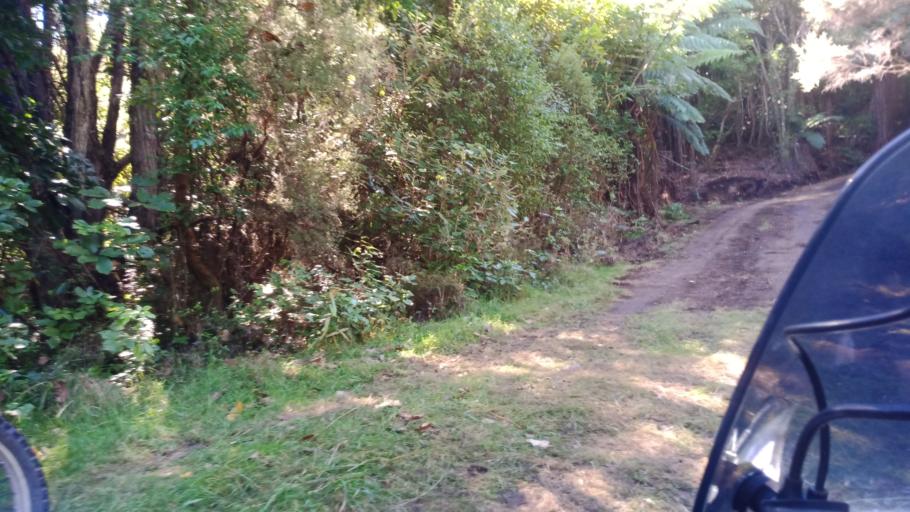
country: NZ
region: Hawke's Bay
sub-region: Wairoa District
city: Wairoa
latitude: -39.0031
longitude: 177.0575
